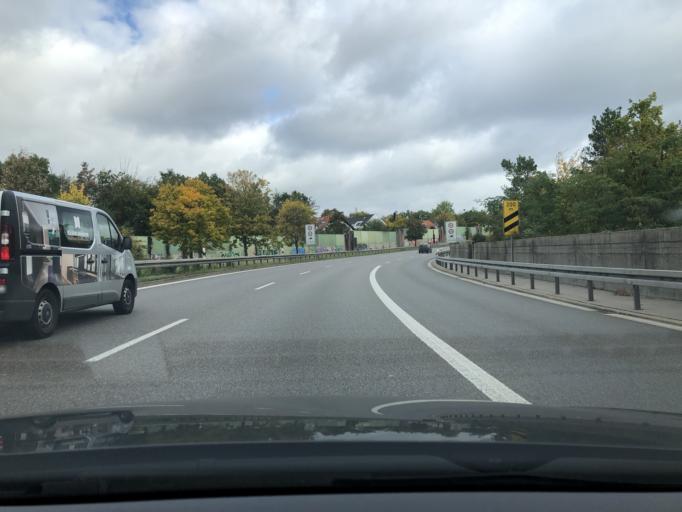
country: DE
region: Baden-Wuerttemberg
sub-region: Regierungsbezirk Stuttgart
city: Gerlingen
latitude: 48.7422
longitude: 9.1105
